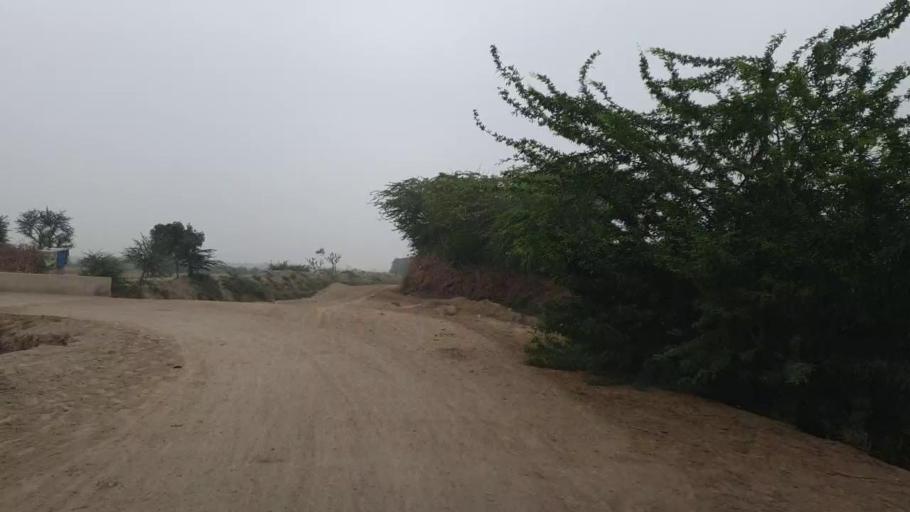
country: PK
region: Sindh
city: Badin
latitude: 24.5988
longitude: 68.6740
